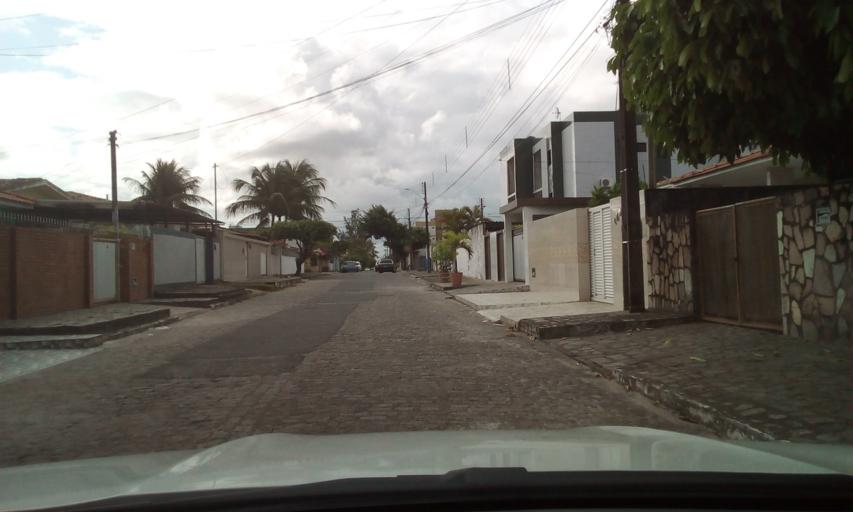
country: BR
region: Paraiba
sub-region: Joao Pessoa
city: Joao Pessoa
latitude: -7.1604
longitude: -34.8740
